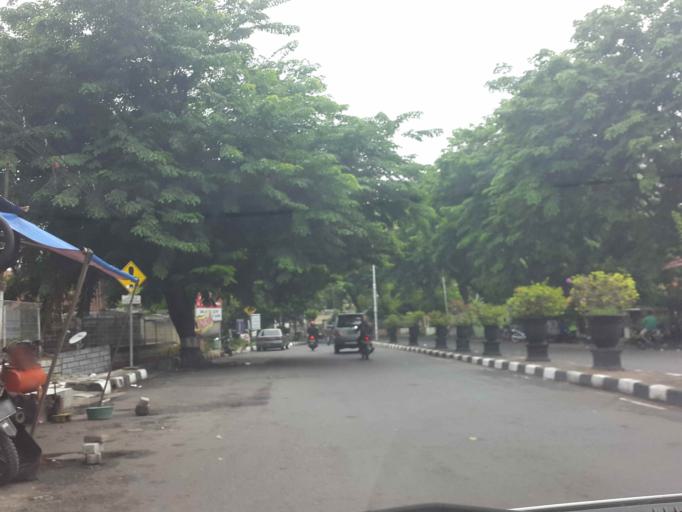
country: ID
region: Central Java
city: Semarang
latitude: -6.9957
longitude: 110.4099
